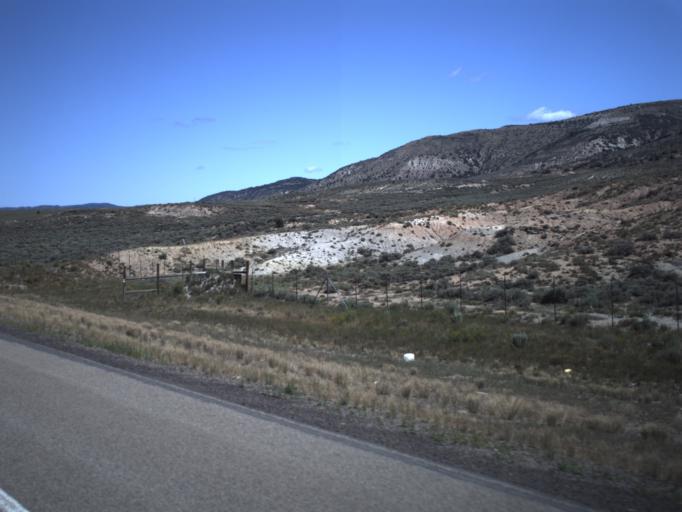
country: US
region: Utah
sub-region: Carbon County
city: Helper
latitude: 39.8544
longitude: -111.0158
